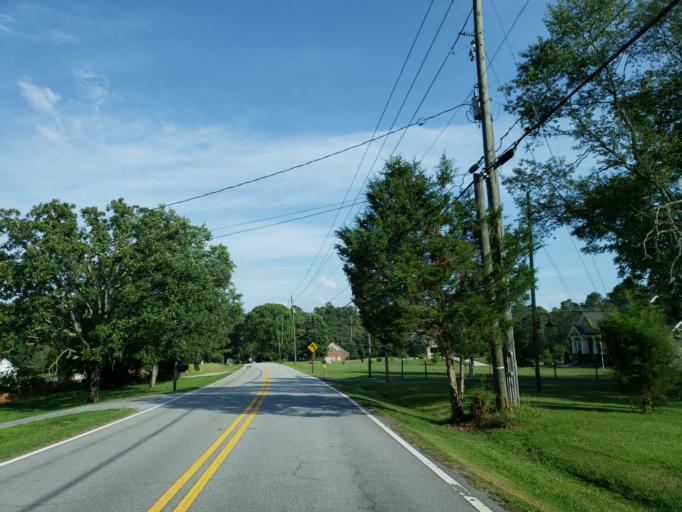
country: US
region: Georgia
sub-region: Paulding County
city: Hiram
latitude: 33.9139
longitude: -84.7170
